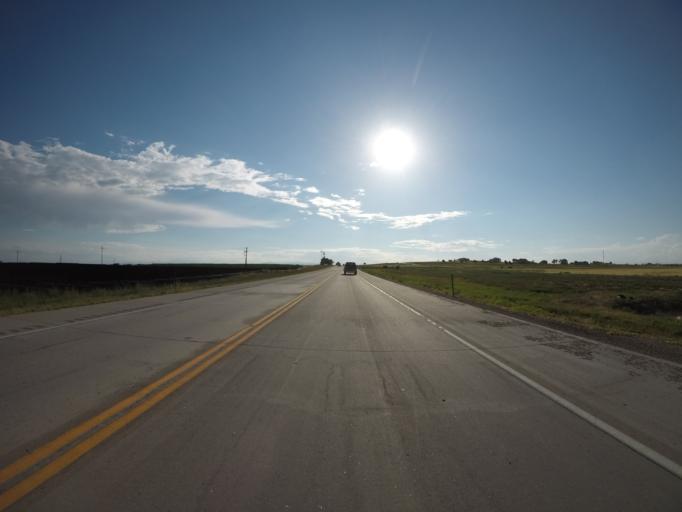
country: US
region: Colorado
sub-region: Weld County
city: Severance
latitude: 40.5815
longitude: -104.8967
